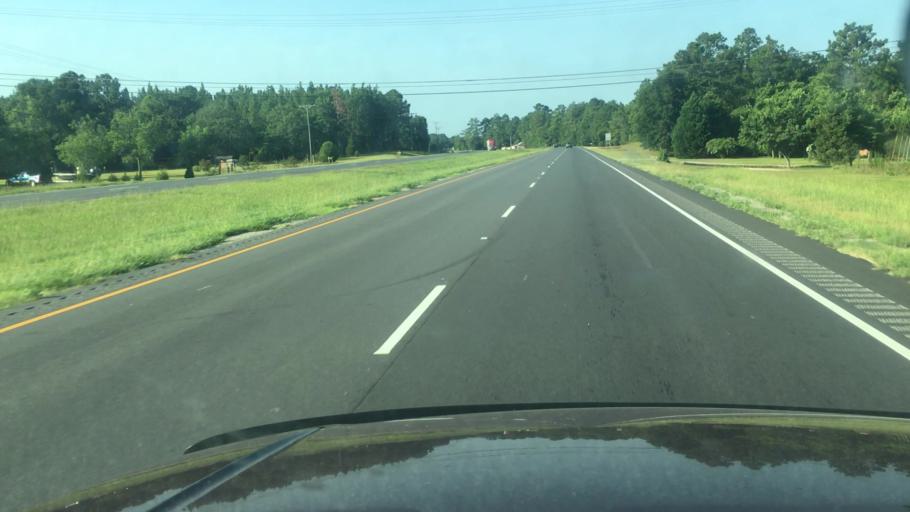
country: US
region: North Carolina
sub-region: Robeson County
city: Saint Pauls
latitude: 34.8705
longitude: -78.8496
